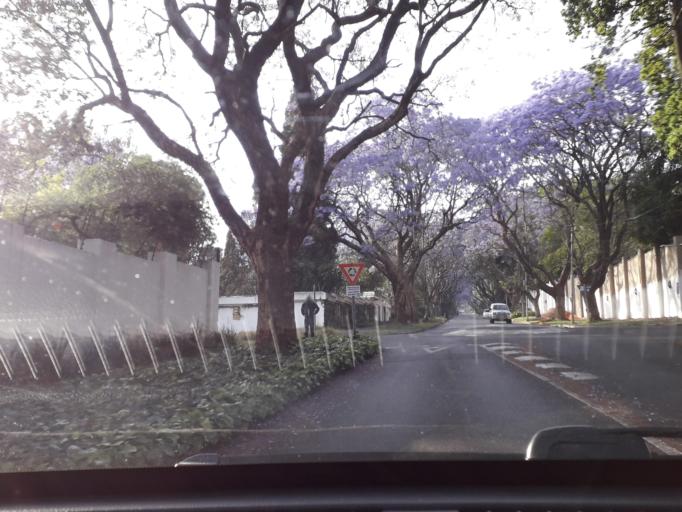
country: ZA
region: Gauteng
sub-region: City of Johannesburg Metropolitan Municipality
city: Johannesburg
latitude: -26.1351
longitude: 28.0771
